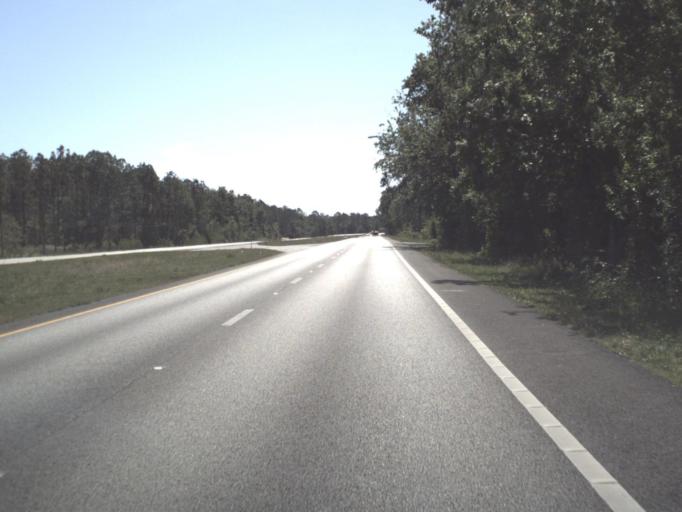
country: US
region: Florida
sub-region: Flagler County
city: Bunnell
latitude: 29.4233
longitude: -81.2169
